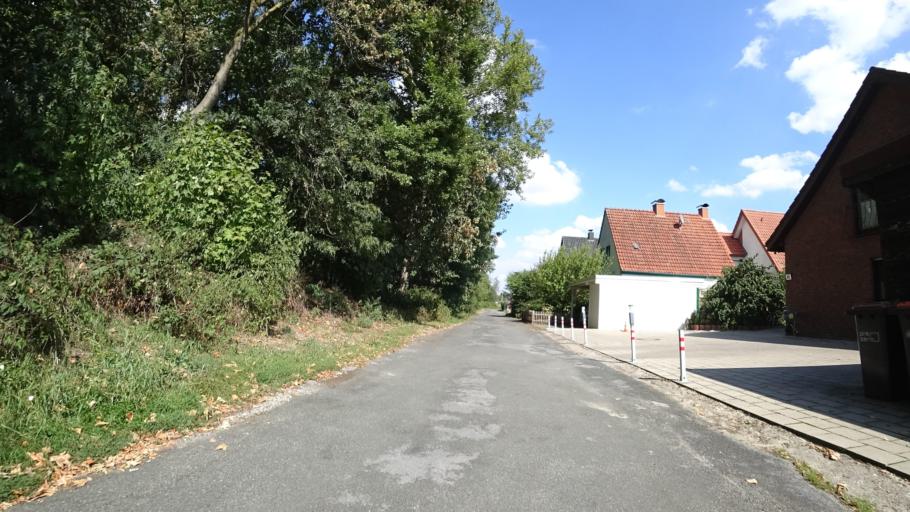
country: DE
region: North Rhine-Westphalia
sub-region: Regierungsbezirk Detmold
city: Rheda-Wiedenbruck
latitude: 51.8662
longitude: 8.2671
